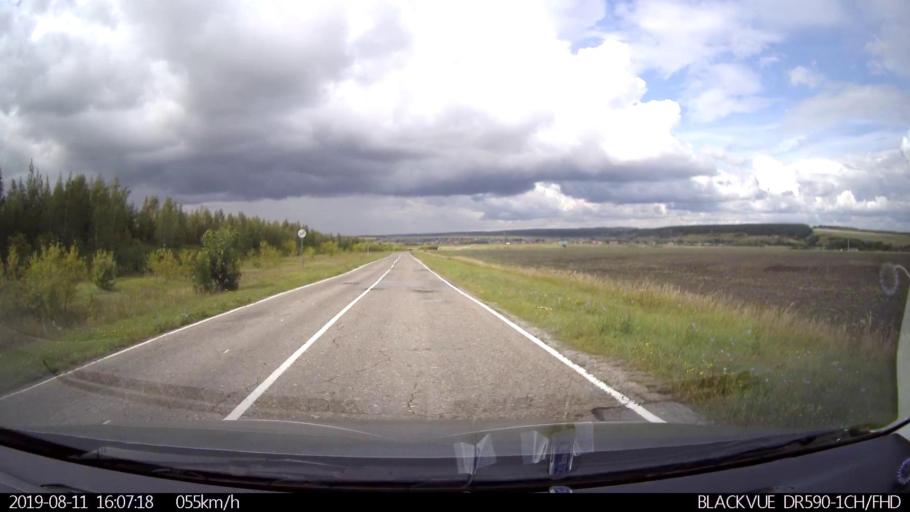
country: RU
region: Ulyanovsk
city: Ignatovka
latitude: 53.9752
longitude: 47.6487
